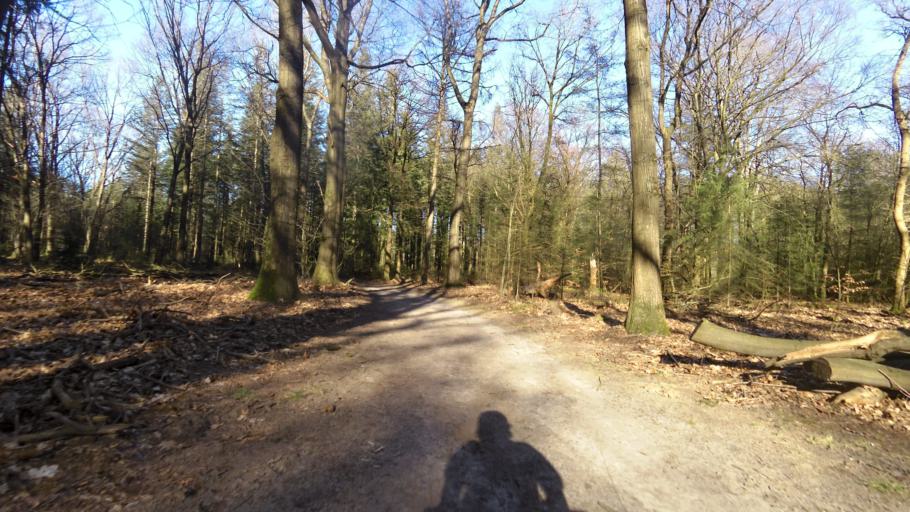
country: NL
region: Gelderland
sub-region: Gemeente Barneveld
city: Garderen
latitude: 52.2212
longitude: 5.6815
